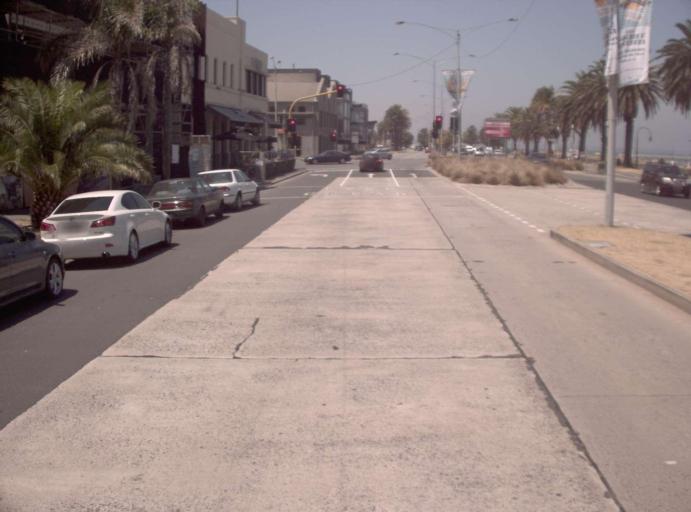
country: AU
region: Victoria
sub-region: Port Phillip
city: Port Melbourne
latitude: -37.8427
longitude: 144.9373
